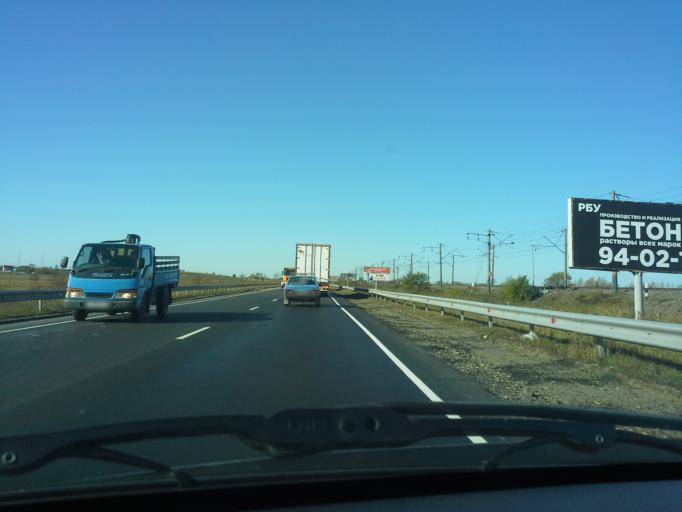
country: RU
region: Jewish Autonomous Oblast
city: Priamurskiy
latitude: 48.5257
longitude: 134.9314
